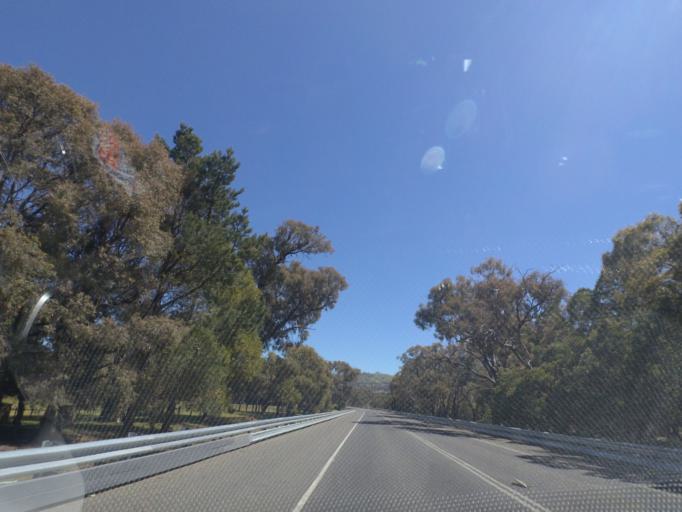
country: AU
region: Victoria
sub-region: Hume
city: Sunbury
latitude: -37.3004
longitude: 144.8263
